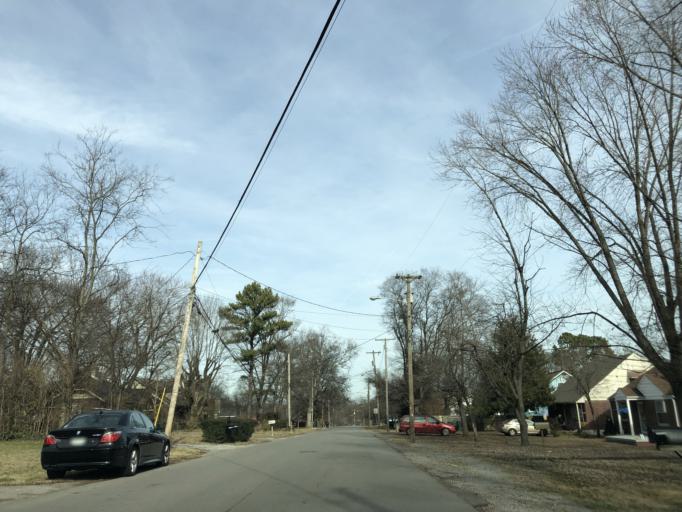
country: US
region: Tennessee
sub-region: Davidson County
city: Nashville
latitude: 36.2153
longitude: -86.7340
